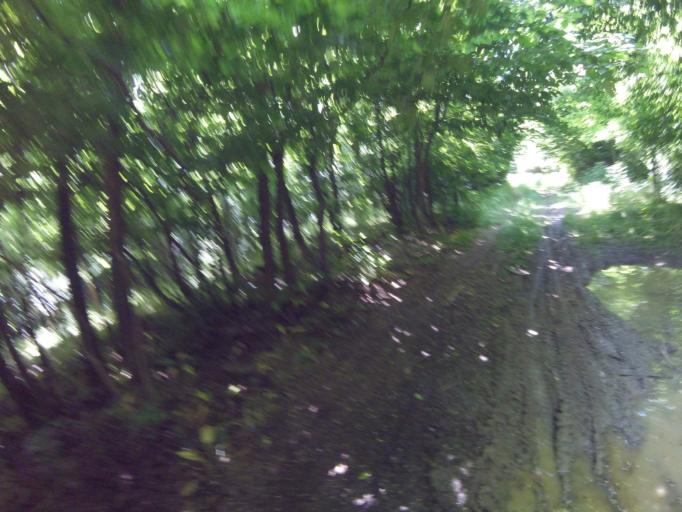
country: HU
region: Zala
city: Zalaszentgrot
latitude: 46.9158
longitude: 17.0424
